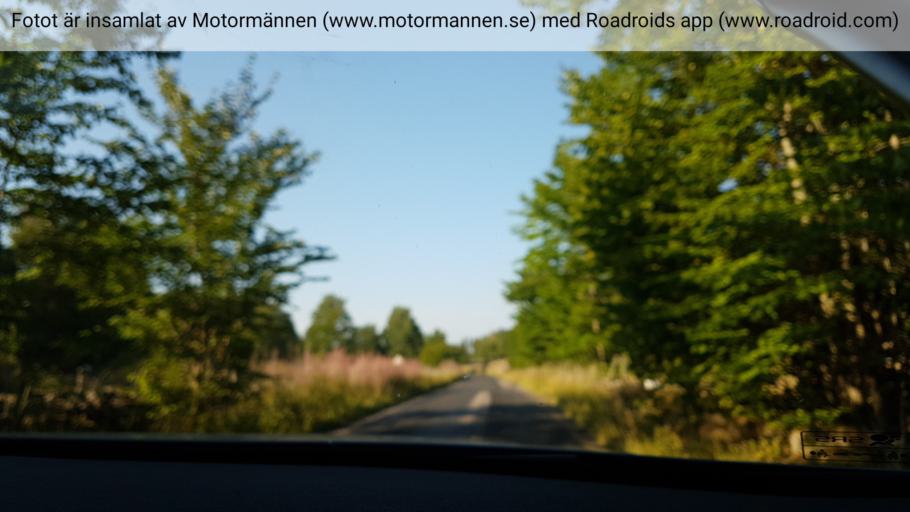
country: SE
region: Vaestra Goetaland
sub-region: Skovde Kommun
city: Skoevde
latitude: 58.4588
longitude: 13.7367
